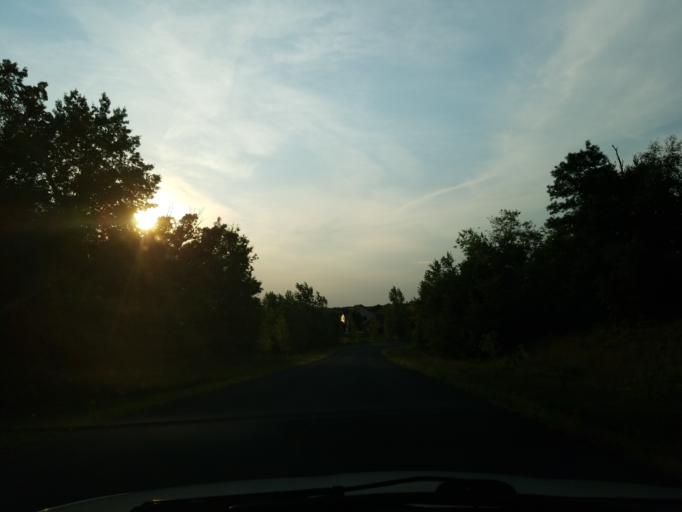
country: US
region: Minnesota
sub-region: Washington County
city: Stillwater
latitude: 45.0678
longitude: -92.7741
